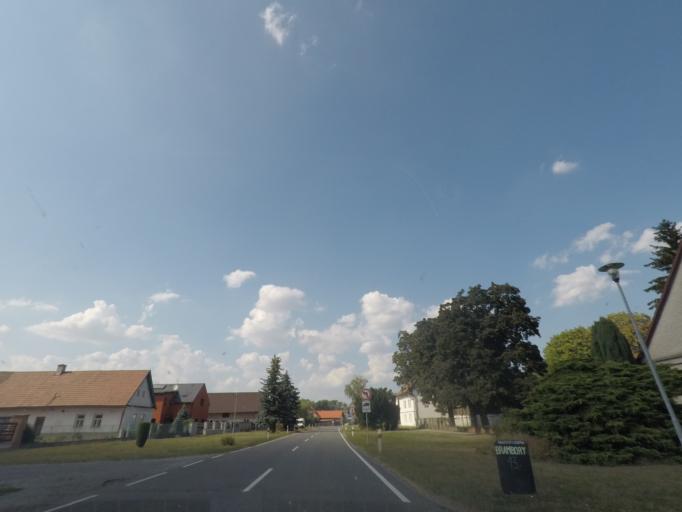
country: CZ
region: Kralovehradecky
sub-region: Okres Nachod
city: Jaromer
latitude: 50.3198
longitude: 15.9492
